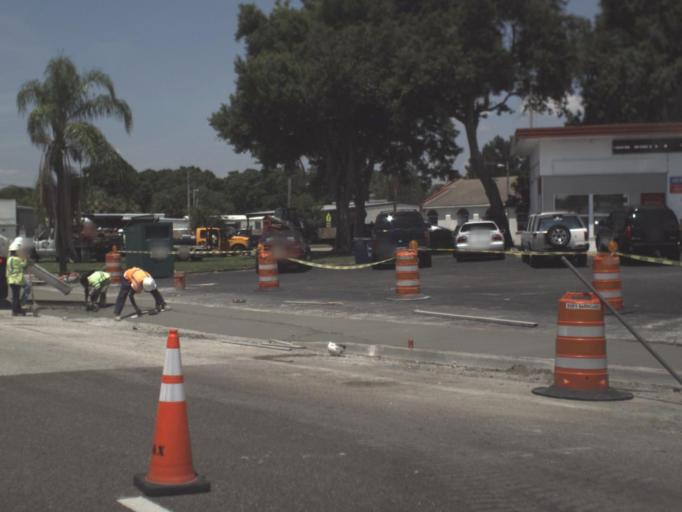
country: US
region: Florida
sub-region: Hillsborough County
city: Ruskin
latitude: 27.7134
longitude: -82.4341
